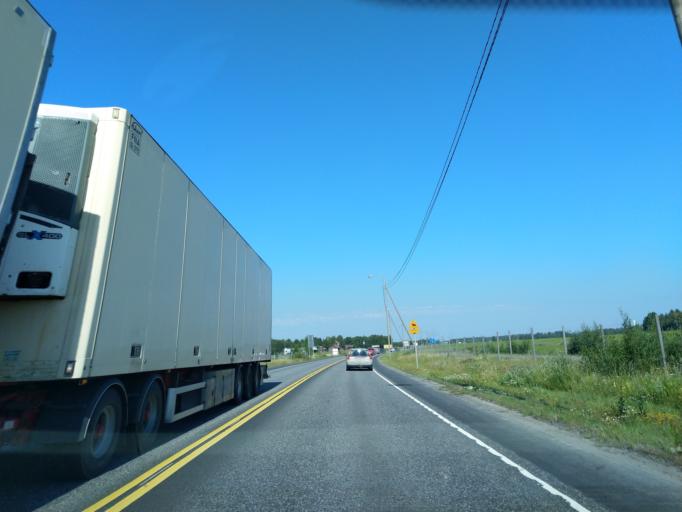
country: FI
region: Satakunta
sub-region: Pori
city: Nakkila
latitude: 61.3462
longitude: 22.0214
